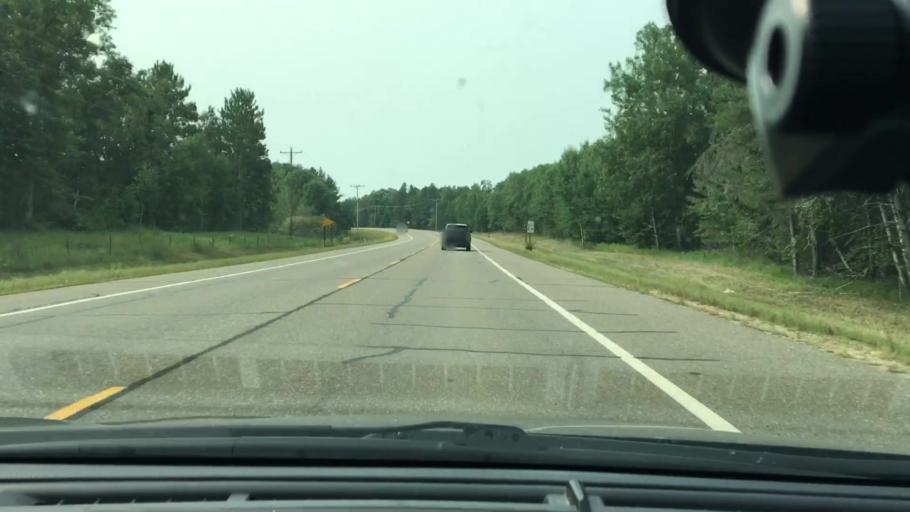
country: US
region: Minnesota
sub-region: Crow Wing County
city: Breezy Point
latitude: 46.5623
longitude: -94.1331
